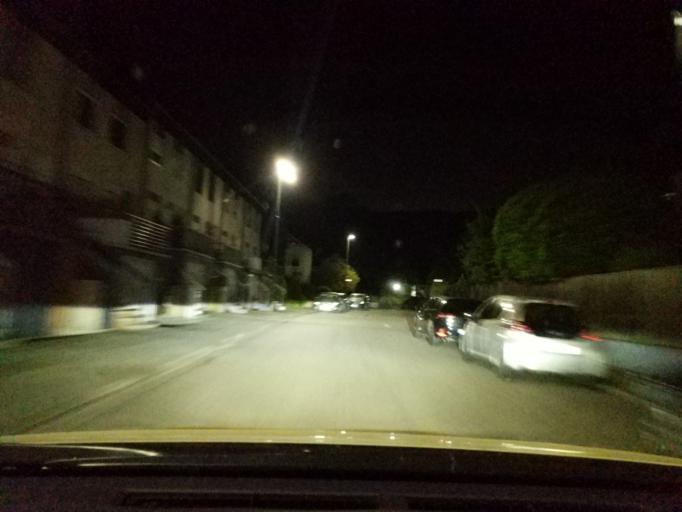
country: DE
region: Rheinland-Pfalz
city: Stelzenberg
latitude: 49.4168
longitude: 7.6940
